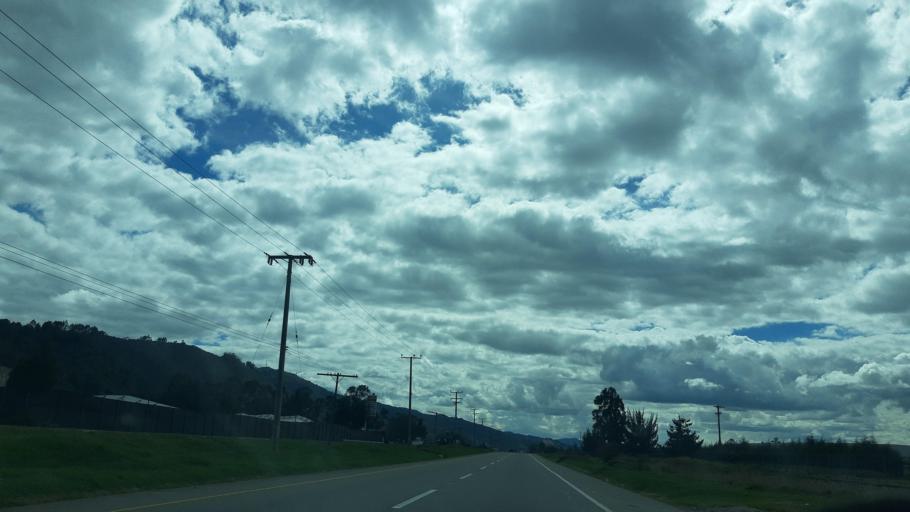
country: CO
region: Cundinamarca
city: Gachancipa
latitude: 5.0144
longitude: -73.8546
